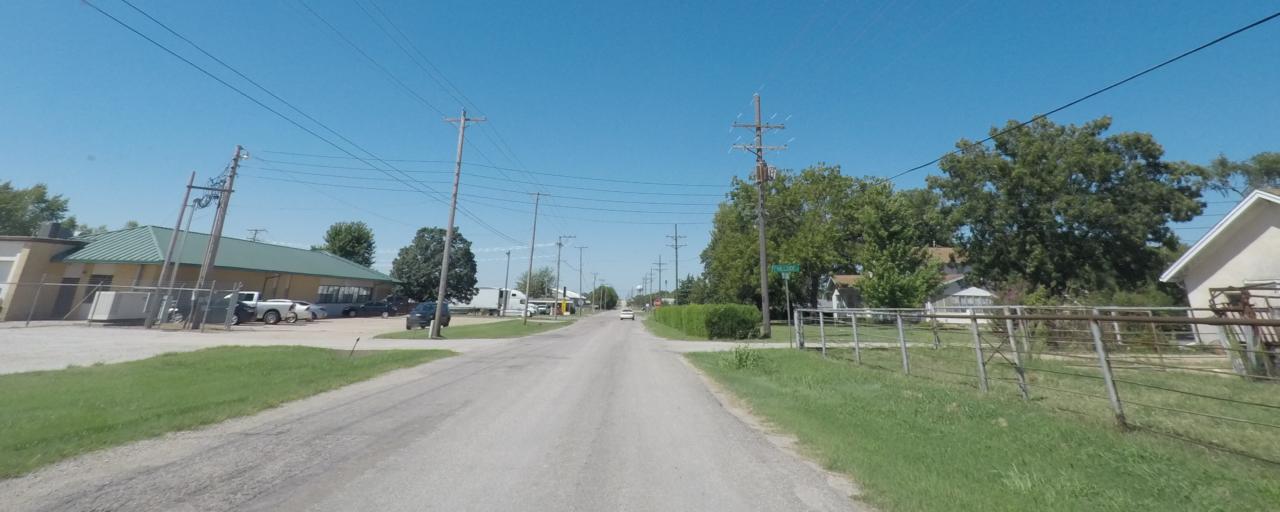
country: US
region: Kansas
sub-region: Sumner County
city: Wellington
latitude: 37.2896
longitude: -97.3930
